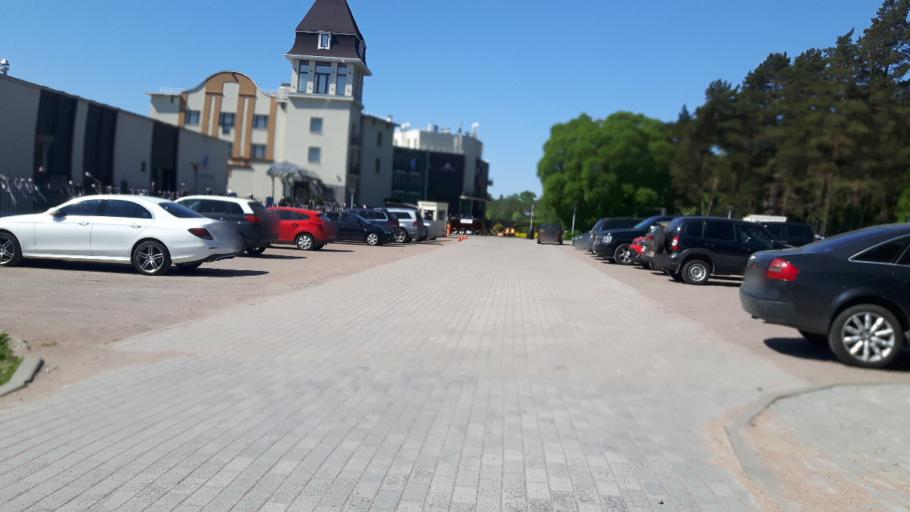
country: RU
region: St.-Petersburg
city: Zelenogorsk
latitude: 60.1881
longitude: 29.7027
